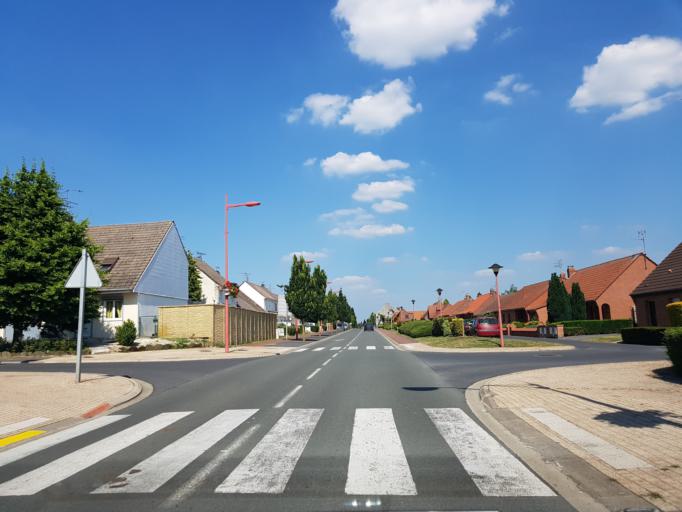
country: FR
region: Nord-Pas-de-Calais
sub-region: Departement du Nord
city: Roeulx
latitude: 50.3075
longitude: 3.3265
